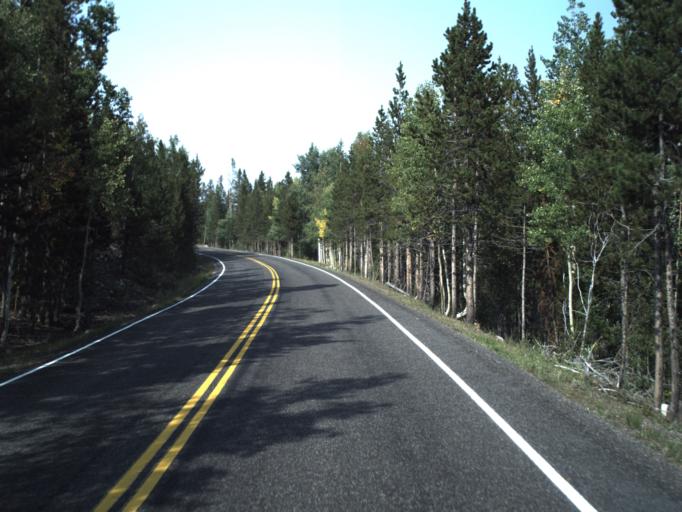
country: US
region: Utah
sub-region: Summit County
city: Oakley
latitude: 40.8084
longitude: -110.8748
